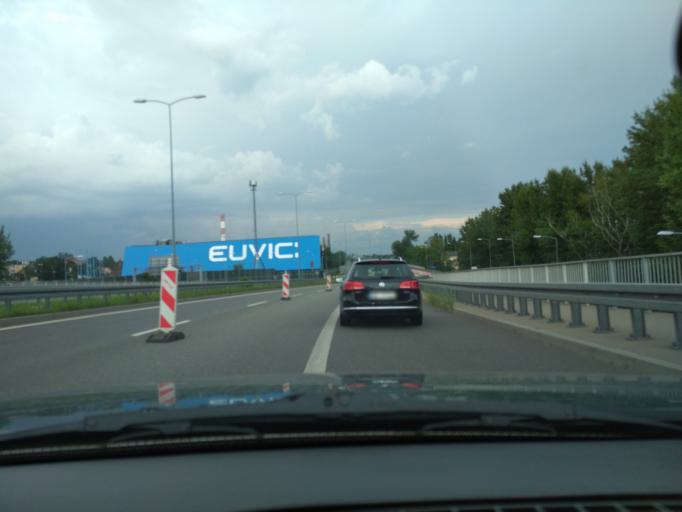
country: PL
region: Silesian Voivodeship
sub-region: Zabrze
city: Zabrze
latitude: 50.2909
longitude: 18.7851
